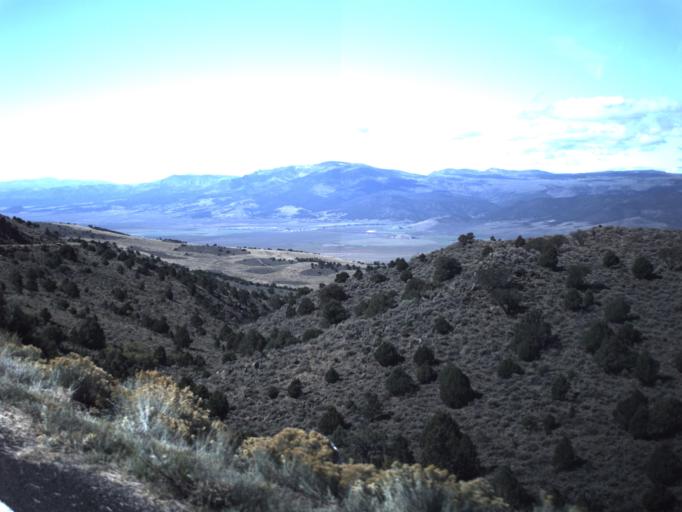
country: US
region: Utah
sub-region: Wayne County
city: Loa
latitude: 38.4817
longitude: -111.8247
